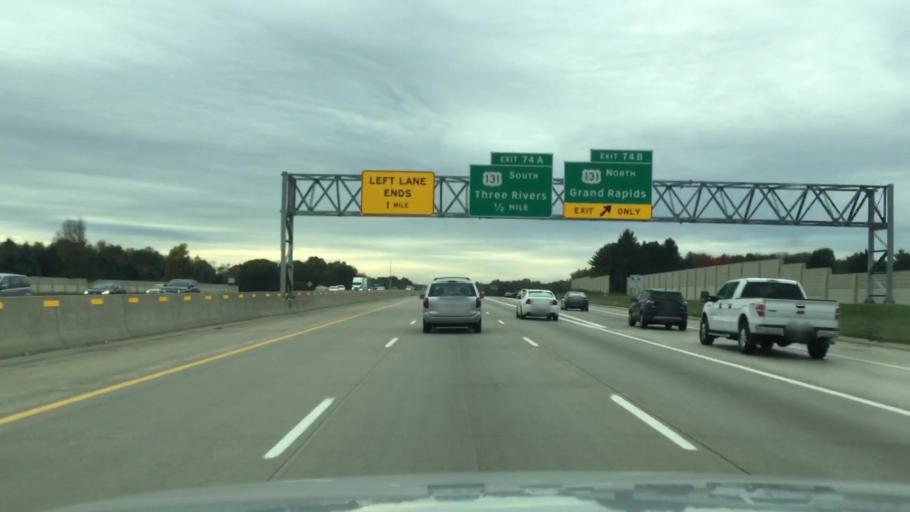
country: US
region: Michigan
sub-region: Kalamazoo County
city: Portage
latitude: 42.2381
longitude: -85.6288
